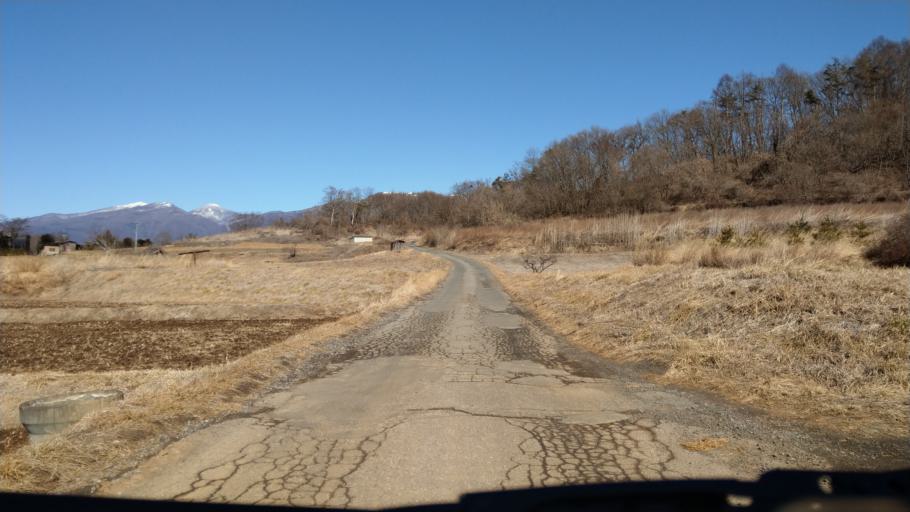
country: JP
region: Nagano
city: Komoro
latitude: 36.3132
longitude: 138.4007
